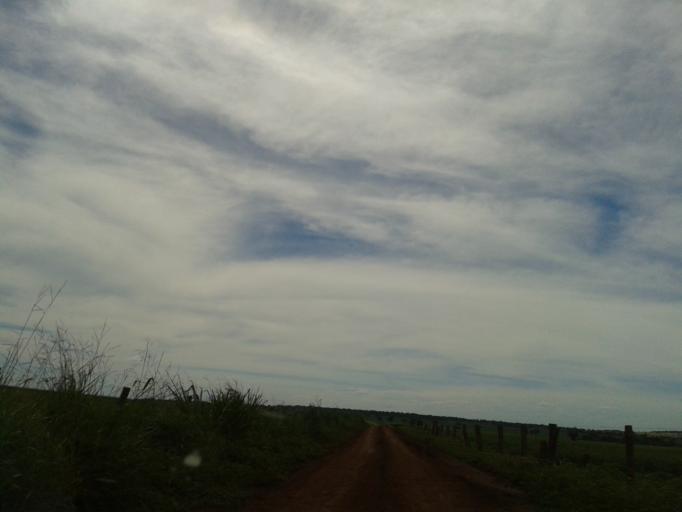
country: BR
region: Minas Gerais
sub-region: Capinopolis
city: Capinopolis
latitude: -18.7476
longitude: -49.8378
